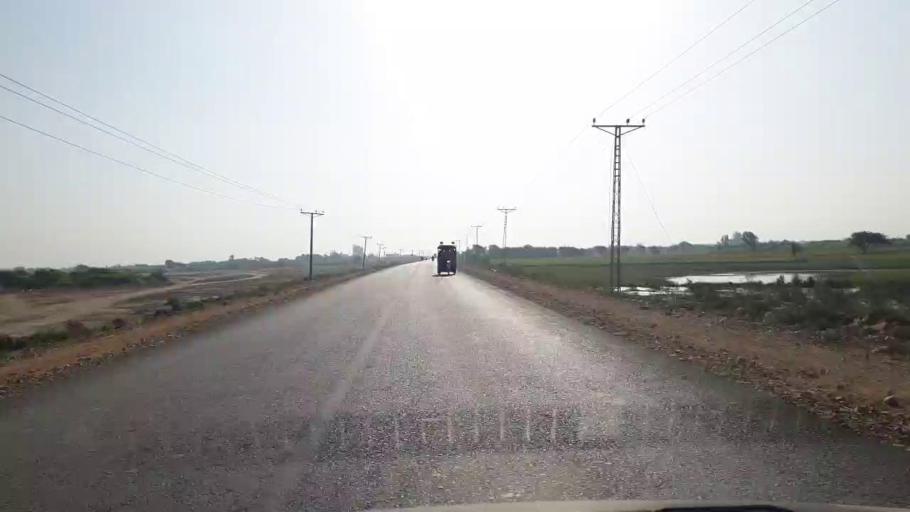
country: PK
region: Sindh
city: Badin
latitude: 24.6653
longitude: 68.8701
